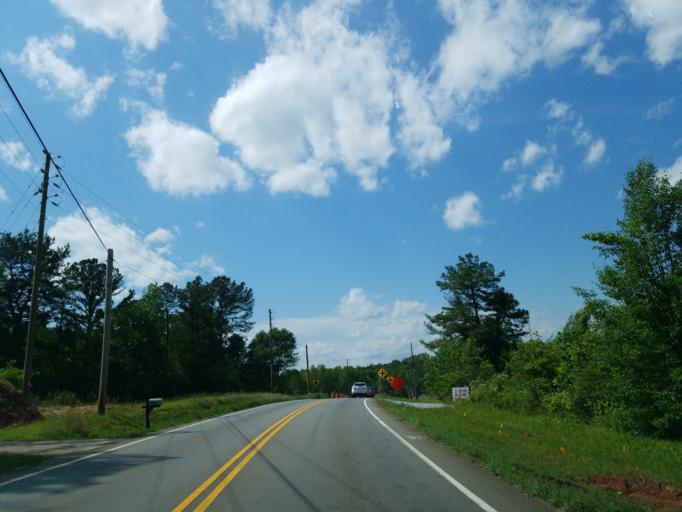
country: US
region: Georgia
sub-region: Cherokee County
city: Ball Ground
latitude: 34.2749
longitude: -84.2982
